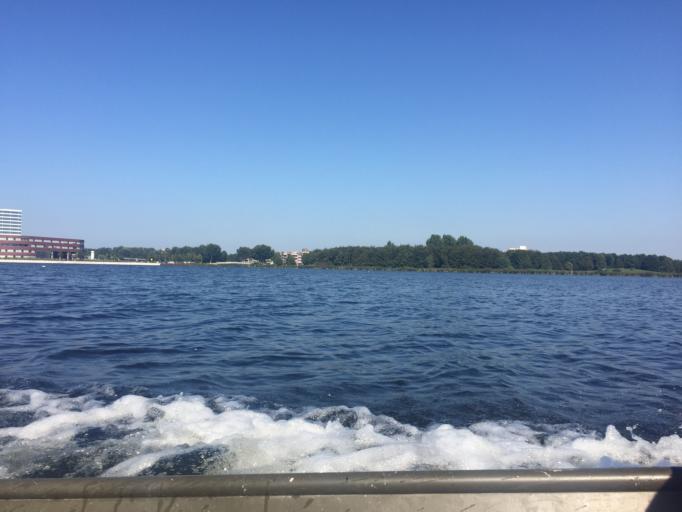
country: NL
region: Flevoland
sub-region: Gemeente Almere
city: Almere Stad
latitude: 52.3643
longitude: 5.2243
